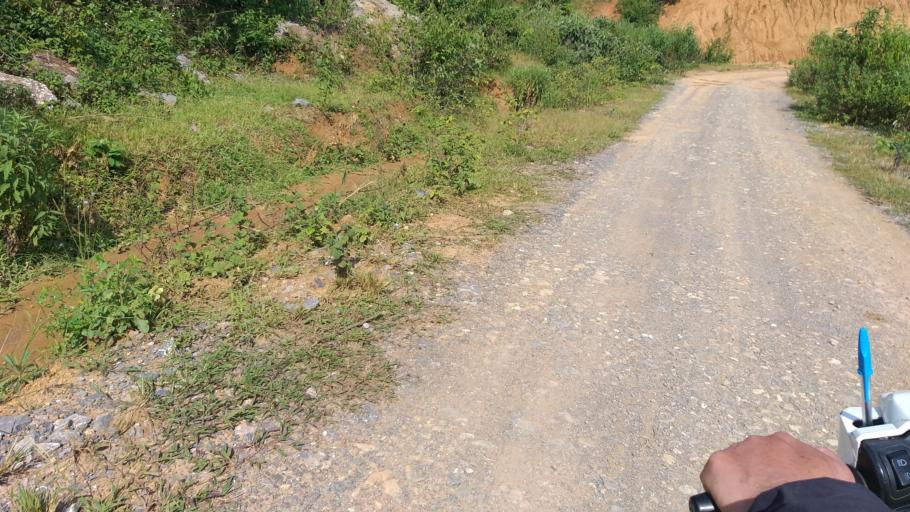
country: LA
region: Phongsali
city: Khoa
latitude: 21.2200
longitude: 102.5992
